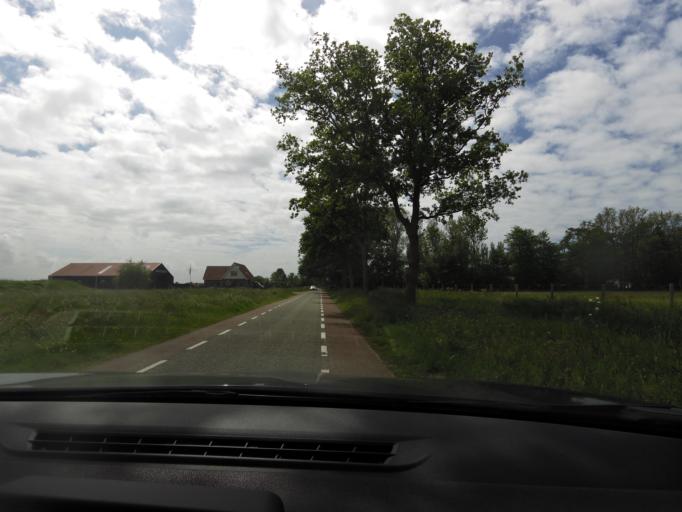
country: NL
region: Zeeland
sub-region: Schouwen-Duiveland
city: Renesse
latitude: 51.7151
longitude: 3.7619
